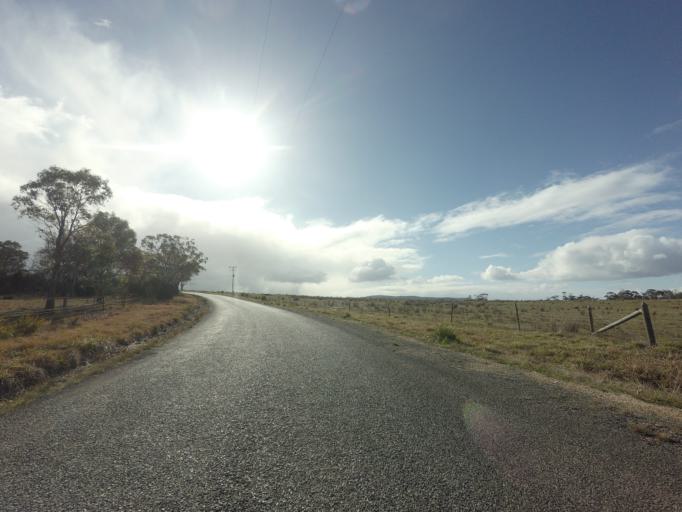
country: AU
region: Tasmania
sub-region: Sorell
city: Sorell
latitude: -42.3024
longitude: 147.9933
